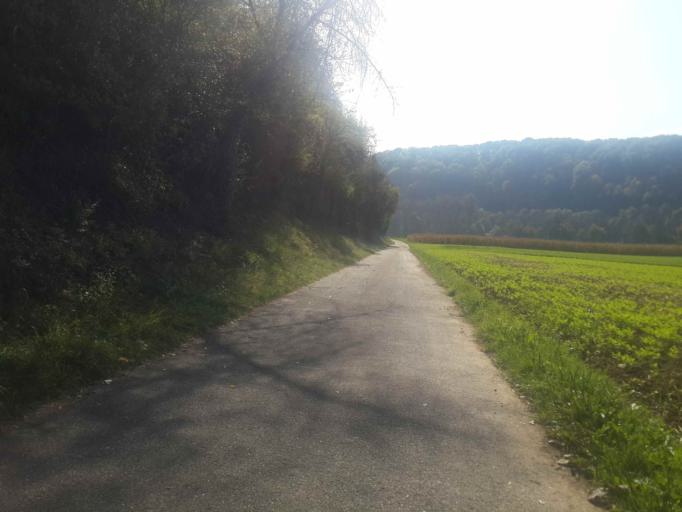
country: DE
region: Baden-Wuerttemberg
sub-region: Regierungsbezirk Stuttgart
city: Neudenau
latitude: 49.2952
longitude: 9.3189
